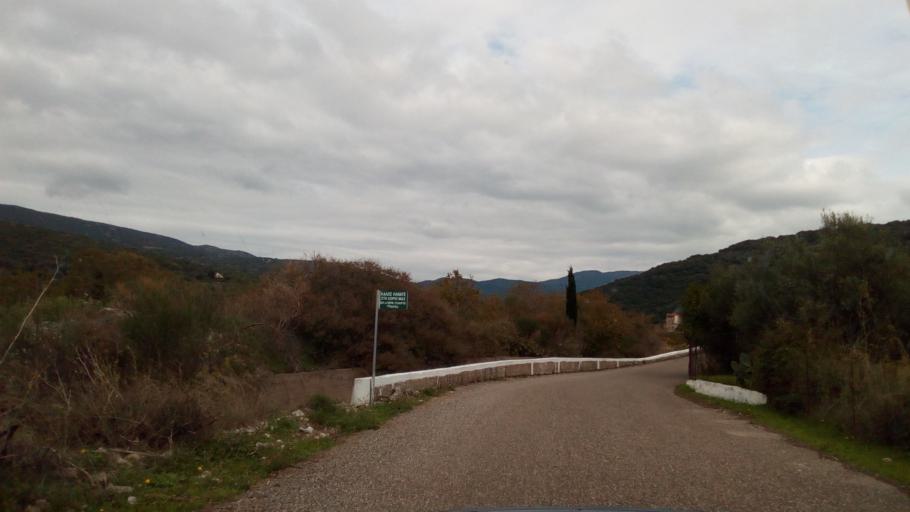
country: GR
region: West Greece
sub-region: Nomos Achaias
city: Kamarai
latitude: 38.4198
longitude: 21.9576
